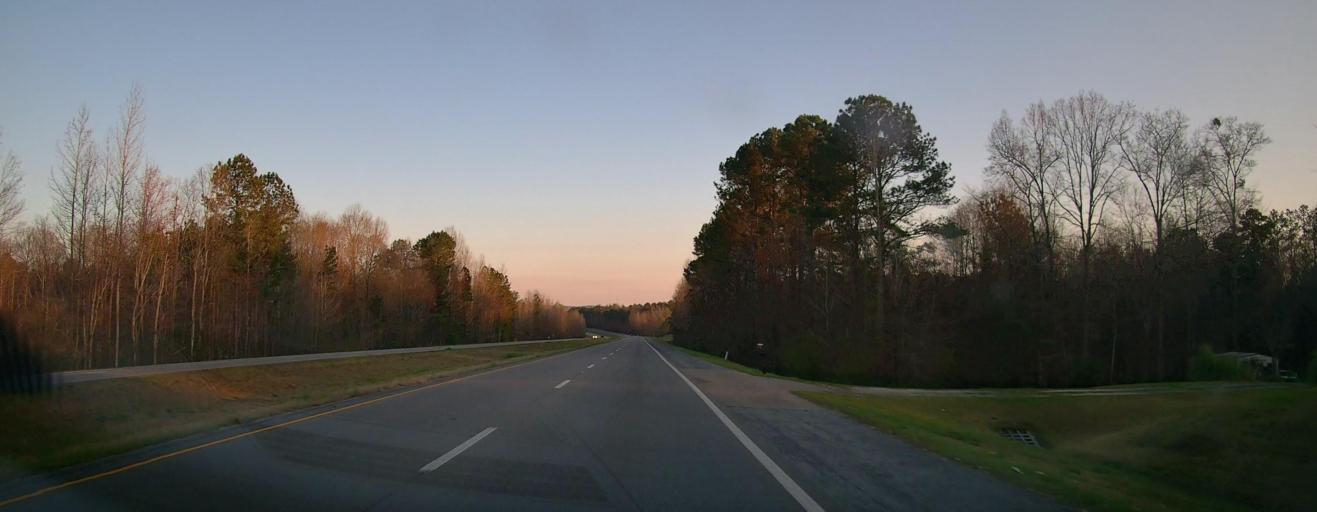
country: US
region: Alabama
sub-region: Coosa County
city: Stewartville
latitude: 33.1214
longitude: -86.2415
